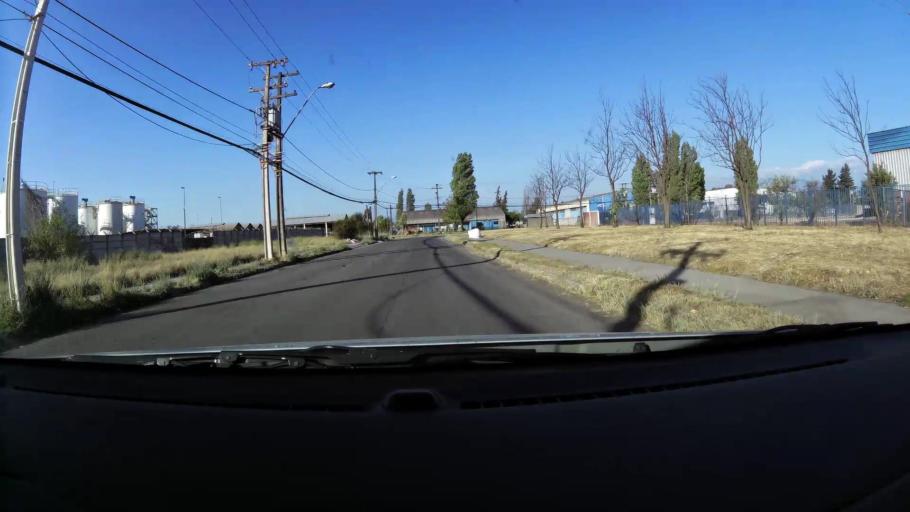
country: CL
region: Santiago Metropolitan
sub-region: Provincia de Maipo
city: San Bernardo
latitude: -33.5331
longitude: -70.7506
